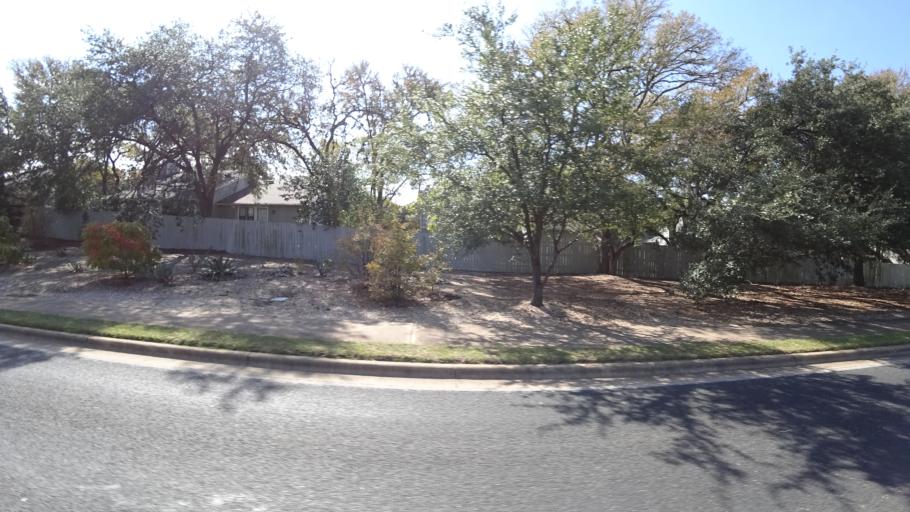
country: US
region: Texas
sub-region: Travis County
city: Shady Hollow
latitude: 30.2114
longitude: -97.8255
